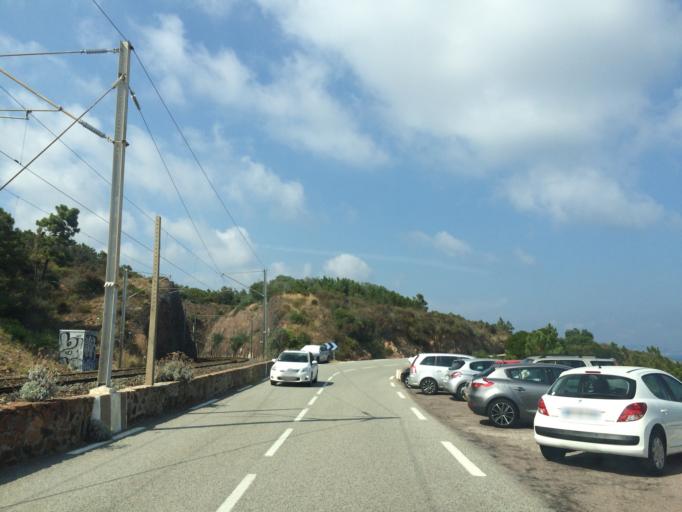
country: FR
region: Provence-Alpes-Cote d'Azur
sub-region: Departement des Alpes-Maritimes
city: Theoule-sur-Mer
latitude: 43.4536
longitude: 6.9201
